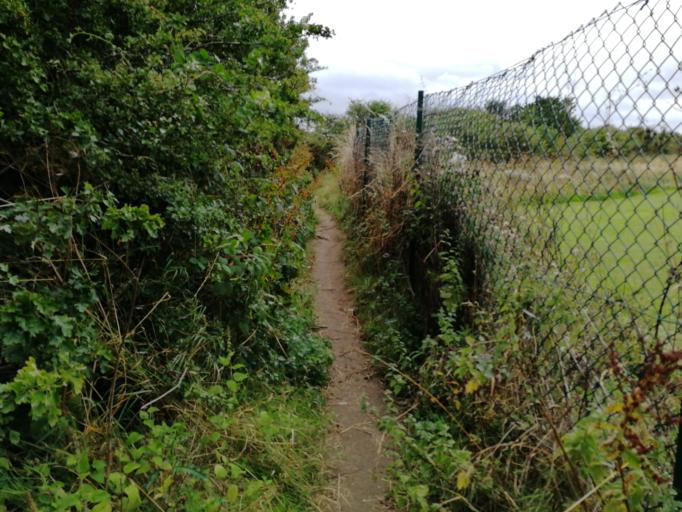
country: GB
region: England
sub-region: North Yorkshire
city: Filey
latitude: 54.2026
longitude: -0.2863
